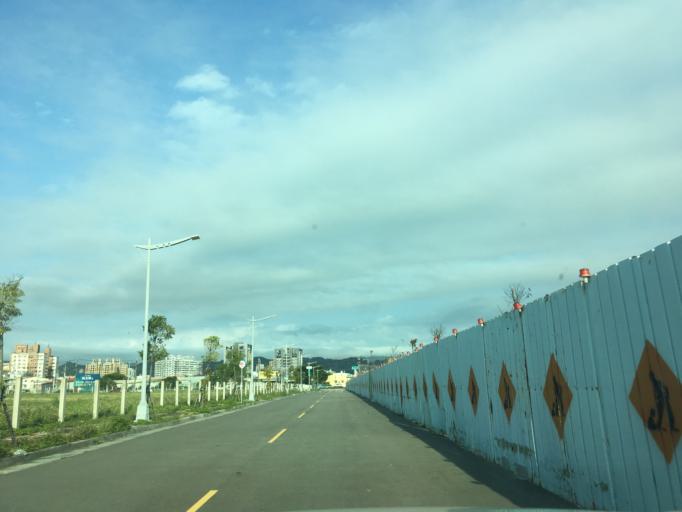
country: TW
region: Taiwan
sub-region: Taichung City
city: Taichung
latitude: 24.1917
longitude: 120.6910
